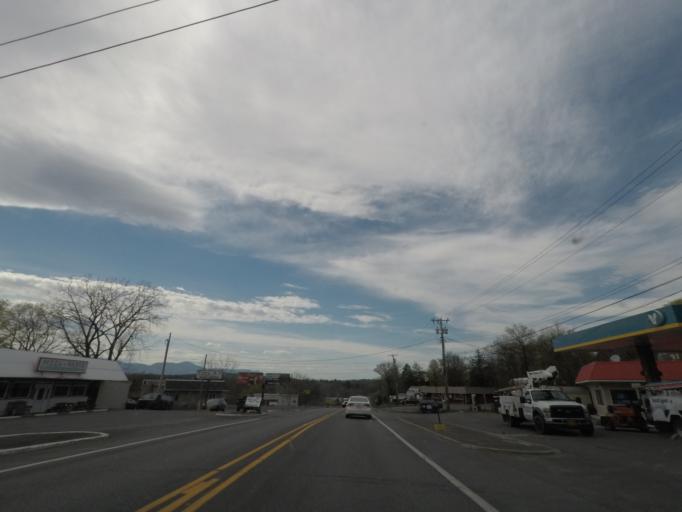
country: US
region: New York
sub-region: Greene County
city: Catskill
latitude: 42.2275
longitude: -73.8632
